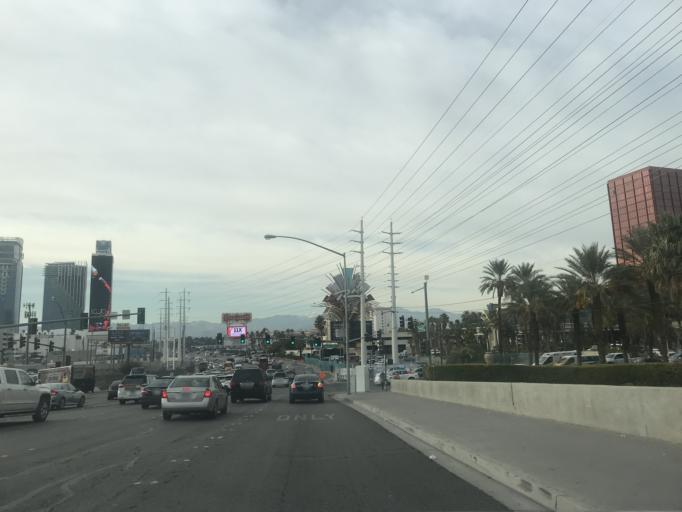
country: US
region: Nevada
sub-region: Clark County
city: Paradise
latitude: 36.1152
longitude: -115.1864
